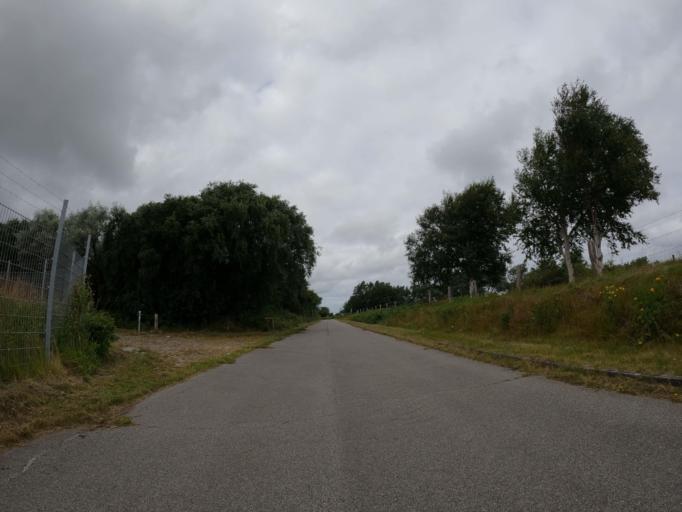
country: DE
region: Schleswig-Holstein
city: Tinnum
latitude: 54.9201
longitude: 8.3466
